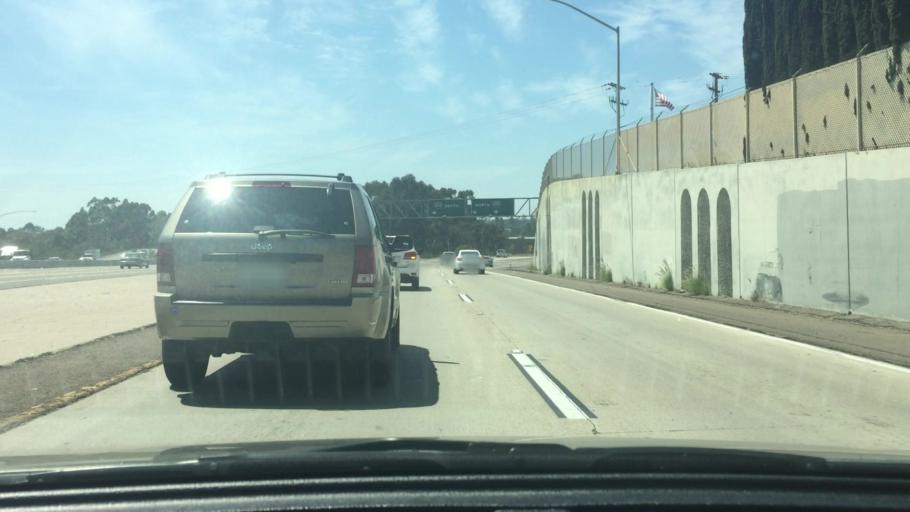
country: US
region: California
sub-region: San Diego County
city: National City
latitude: 32.7195
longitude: -117.0982
